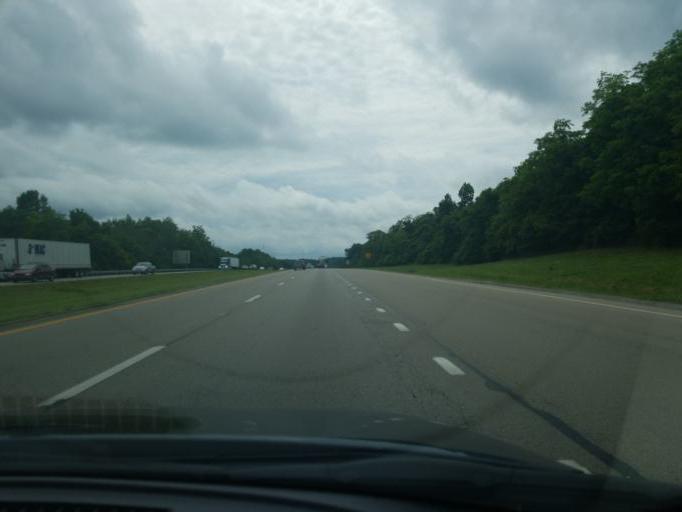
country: US
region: Kentucky
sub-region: Gallatin County
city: Warsaw
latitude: 38.6878
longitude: -84.9480
